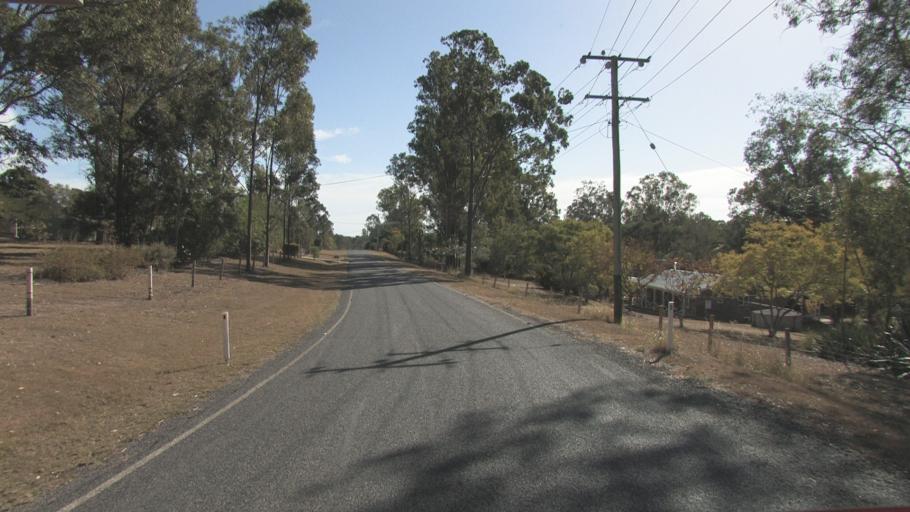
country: AU
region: Queensland
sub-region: Logan
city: Cedar Vale
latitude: -27.8760
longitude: 152.9850
